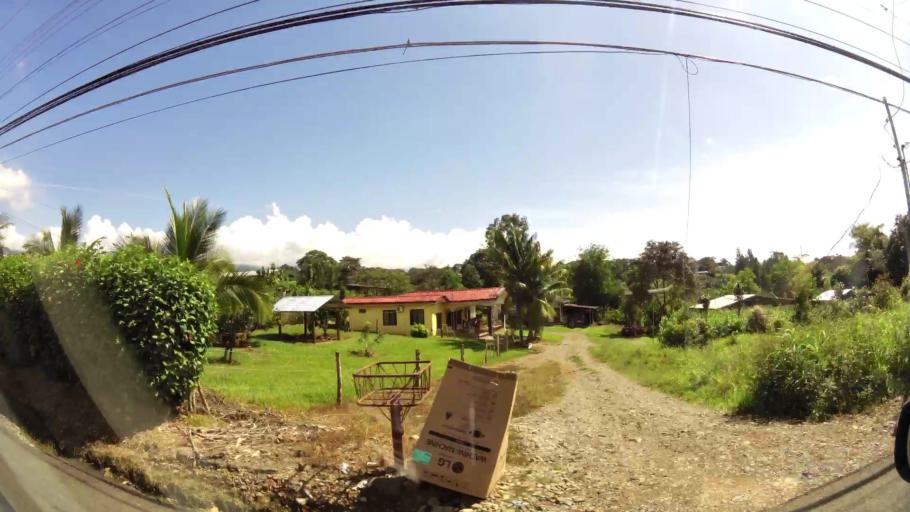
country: CR
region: San Jose
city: San Isidro
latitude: 9.3779
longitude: -83.6978
